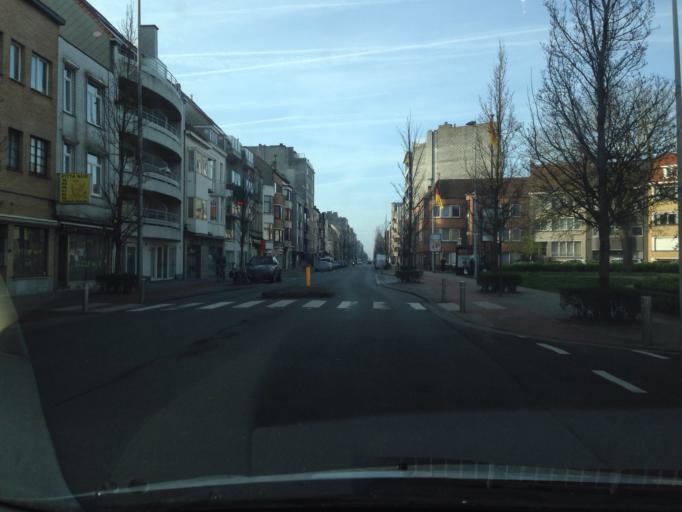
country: BE
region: Flanders
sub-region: Provincie West-Vlaanderen
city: Ostend
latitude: 51.2216
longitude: 2.9084
